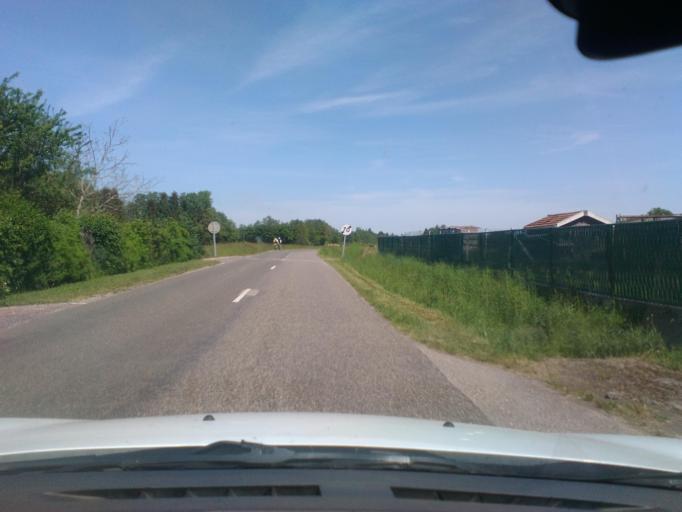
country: FR
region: Lorraine
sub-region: Departement des Vosges
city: Jeanmenil
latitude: 48.3013
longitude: 6.6850
